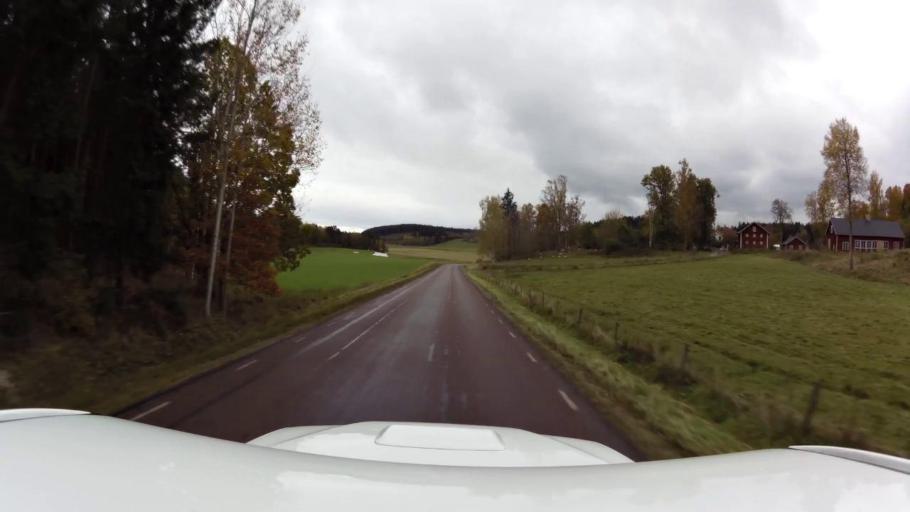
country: SE
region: OEstergoetland
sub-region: Linkopings Kommun
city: Ljungsbro
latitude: 58.5589
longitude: 15.5182
